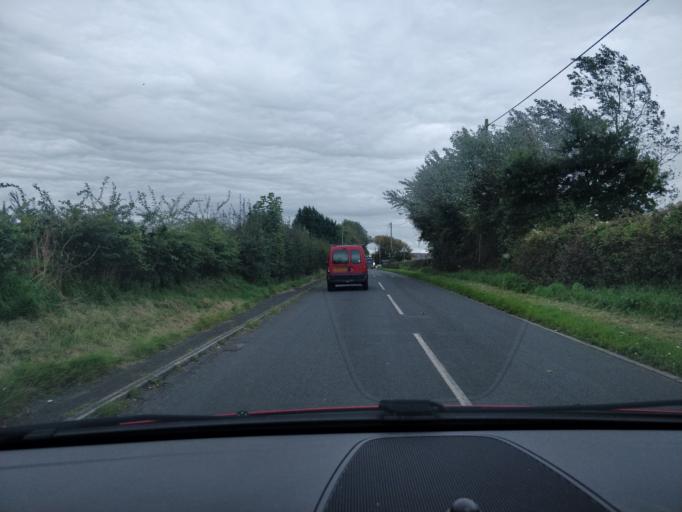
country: GB
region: England
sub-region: Lancashire
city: Ormskirk
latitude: 53.6211
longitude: -2.8577
